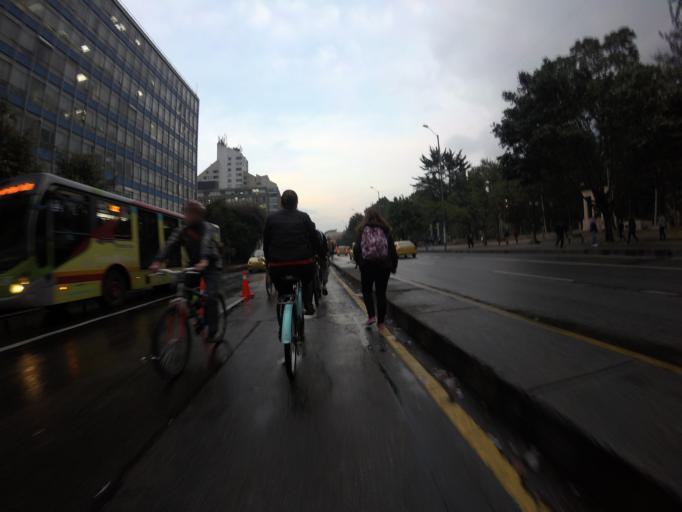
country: CO
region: Bogota D.C.
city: Bogota
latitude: 4.6236
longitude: -74.0664
